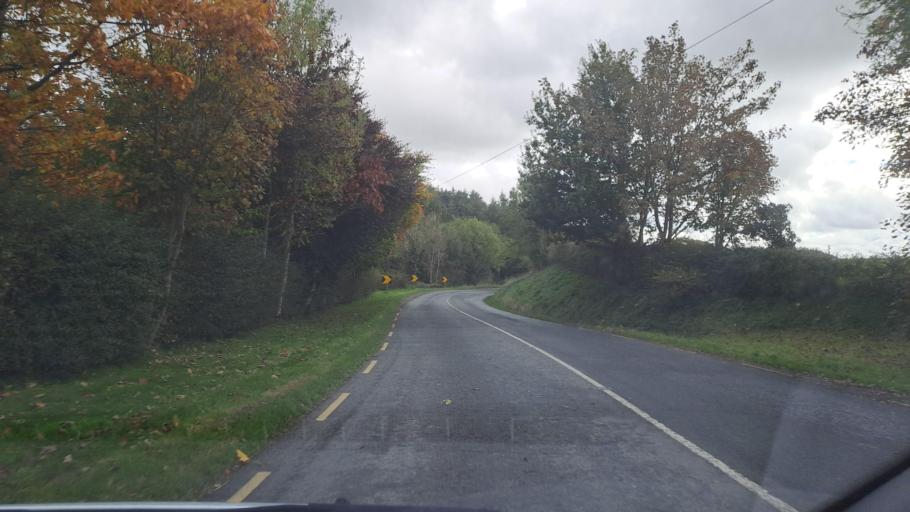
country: IE
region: Ulster
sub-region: An Cabhan
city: Mullagh
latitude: 53.8207
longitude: -7.0034
